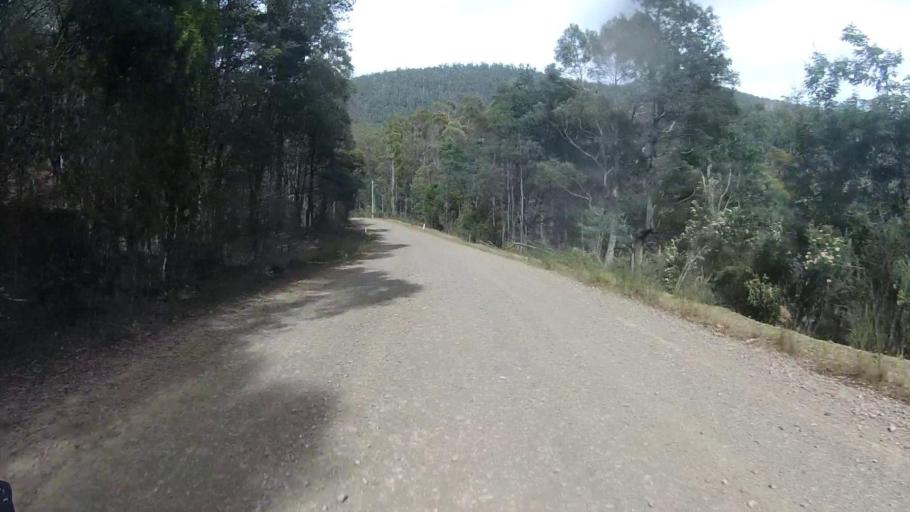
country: AU
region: Tasmania
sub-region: Sorell
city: Sorell
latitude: -42.6896
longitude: 147.8667
